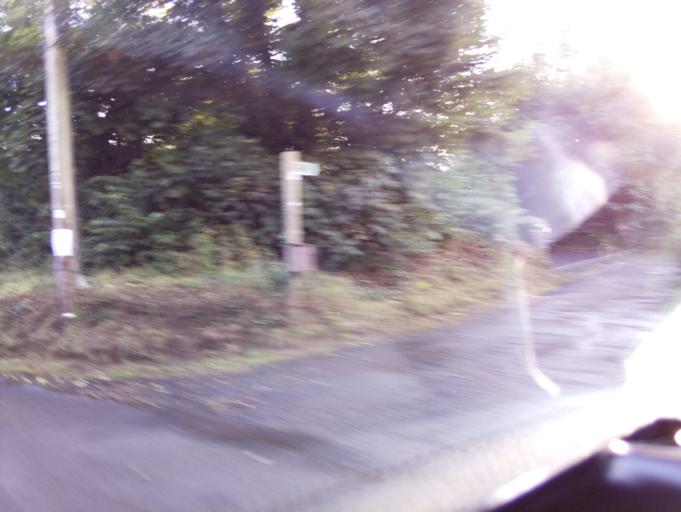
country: GB
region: England
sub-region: Devon
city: Totnes
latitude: 50.3460
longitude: -3.6911
